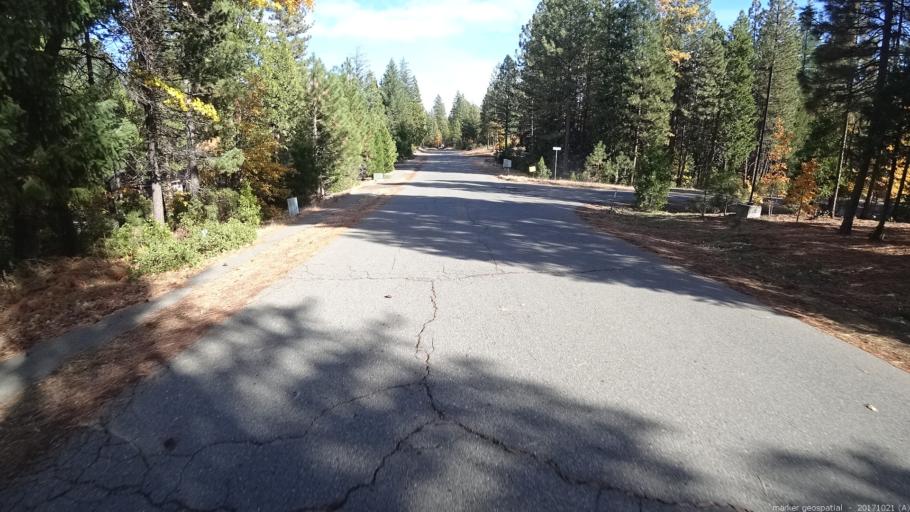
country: US
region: California
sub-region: Shasta County
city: Burney
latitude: 40.8744
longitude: -121.6592
